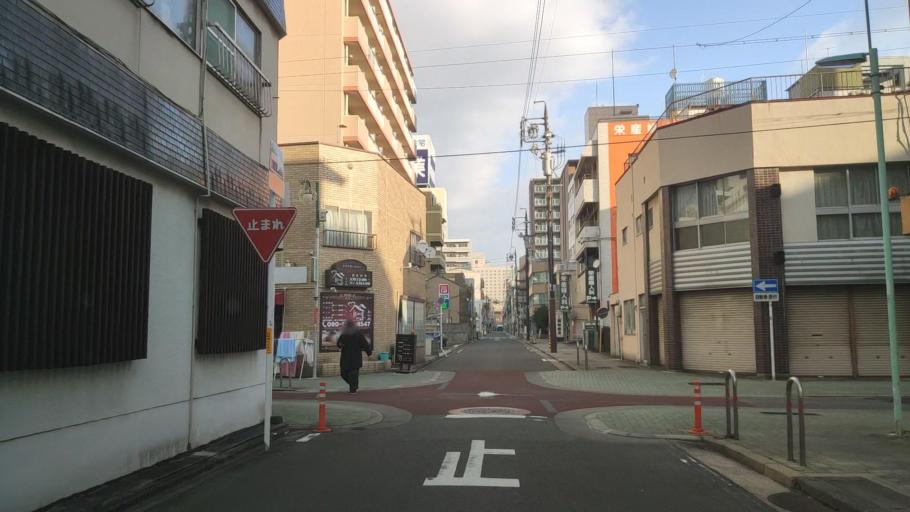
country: JP
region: Aichi
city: Nagoya-shi
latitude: 35.1626
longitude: 136.9145
